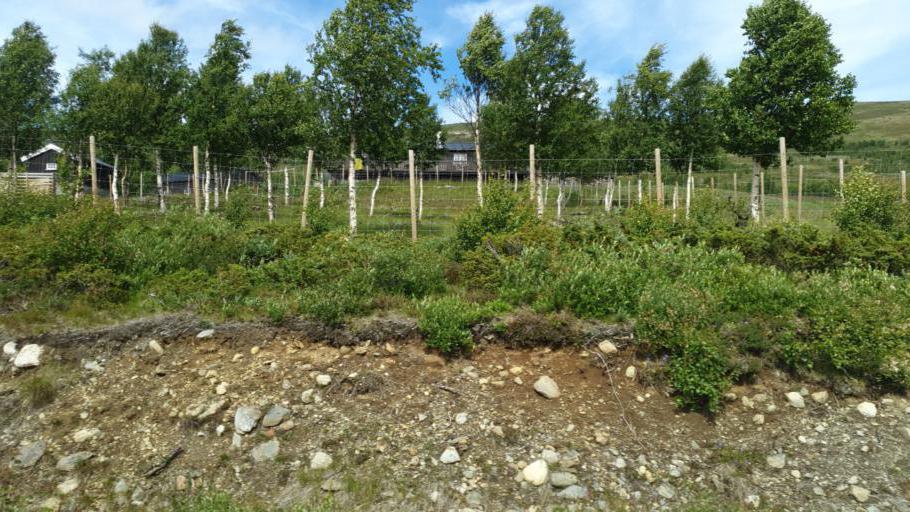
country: NO
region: Oppland
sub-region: Oystre Slidre
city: Heggenes
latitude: 61.5151
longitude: 8.8556
